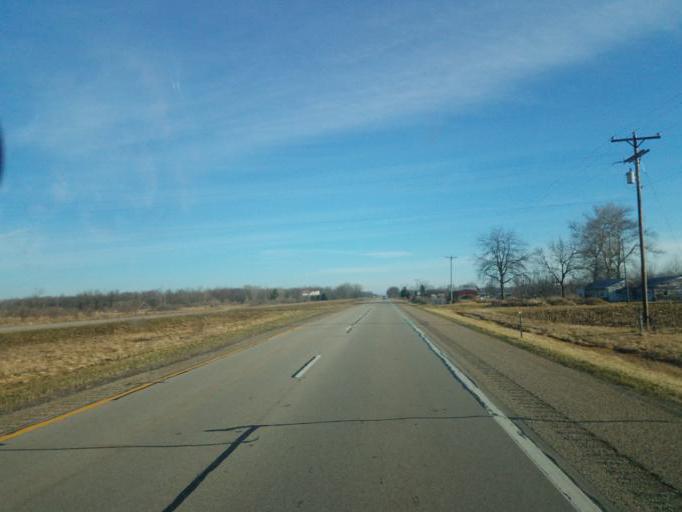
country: US
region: Michigan
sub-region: Clinton County
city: Saint Johns
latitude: 43.1310
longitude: -84.5632
